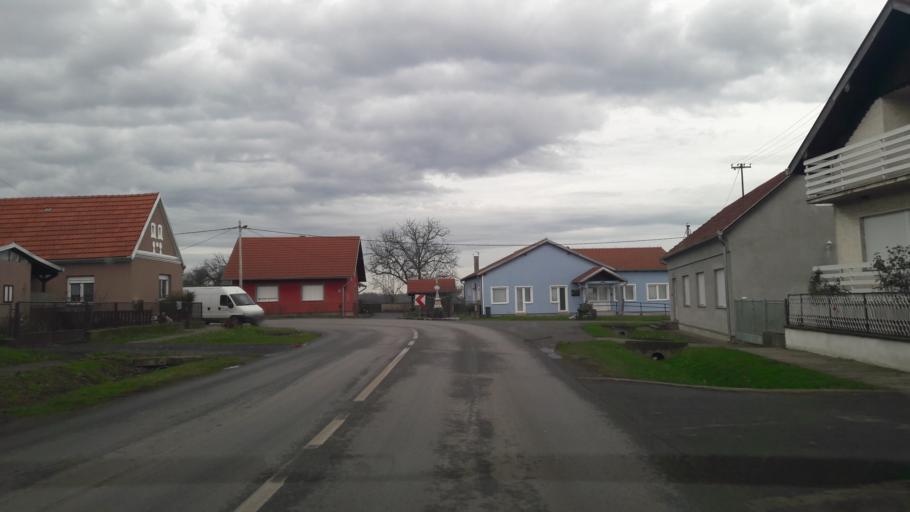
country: HR
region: Osjecko-Baranjska
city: Velimirovac
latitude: 45.5360
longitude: 18.0837
